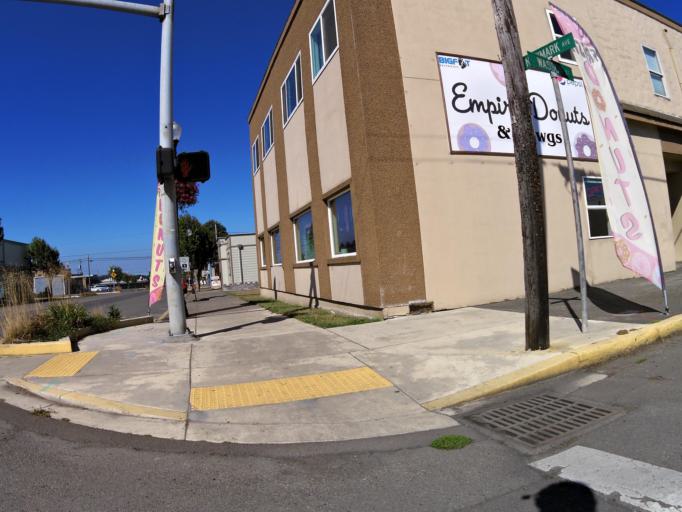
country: US
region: Oregon
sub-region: Coos County
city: North Bend
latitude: 43.3922
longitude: -124.2741
